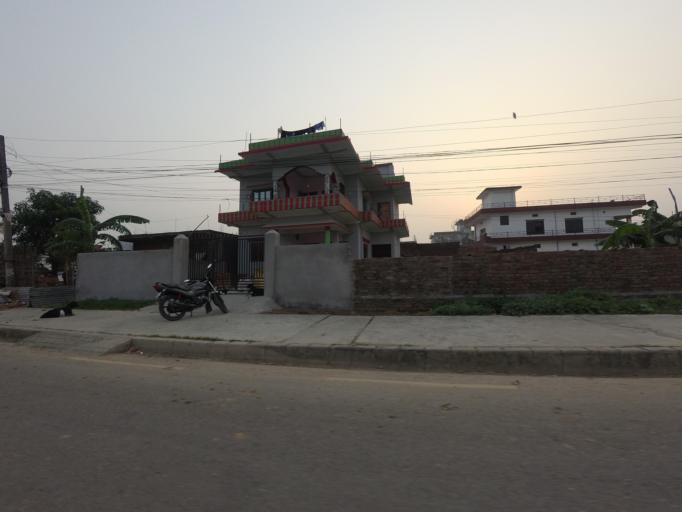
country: NP
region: Western Region
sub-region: Lumbini Zone
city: Bhairahawa
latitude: 27.4977
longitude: 83.4614
